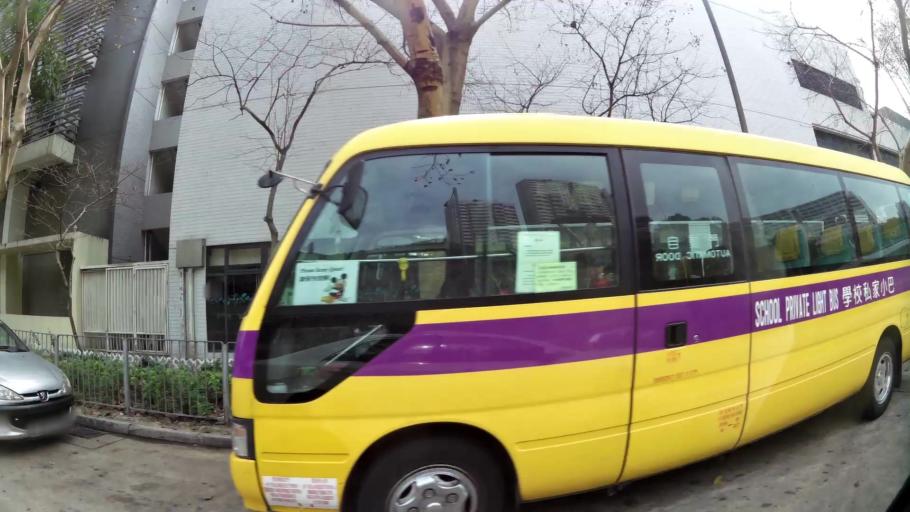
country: HK
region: Wanchai
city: Wan Chai
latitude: 22.2718
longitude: 114.2394
